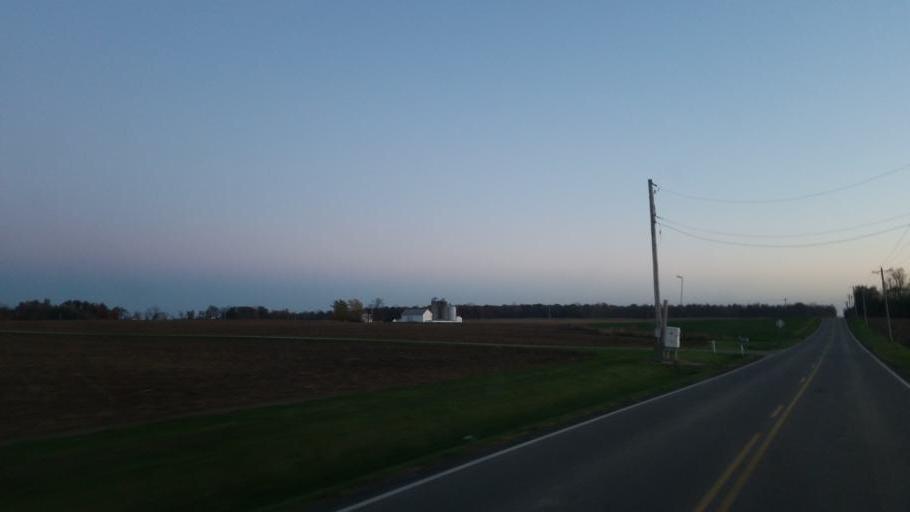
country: US
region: Ohio
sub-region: Richland County
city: Shelby
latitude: 40.9269
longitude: -82.7434
